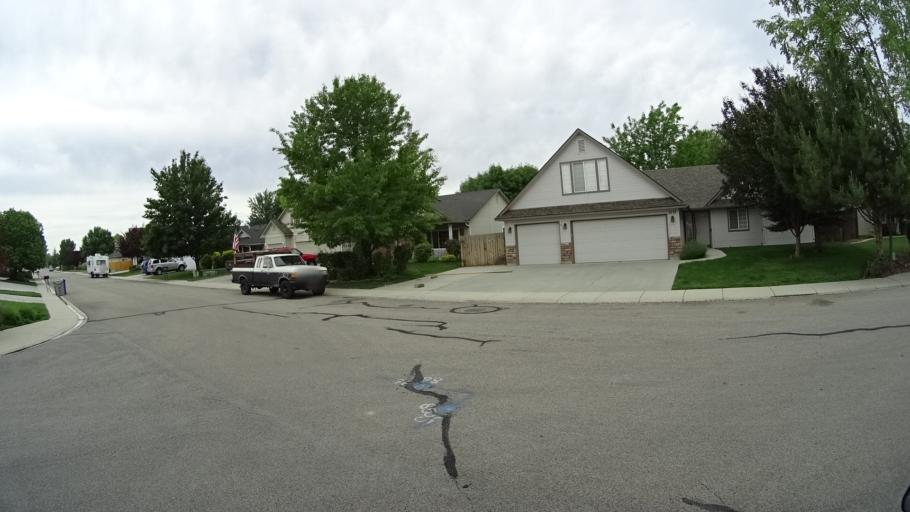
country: US
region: Idaho
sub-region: Ada County
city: Meridian
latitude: 43.5838
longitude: -116.3247
